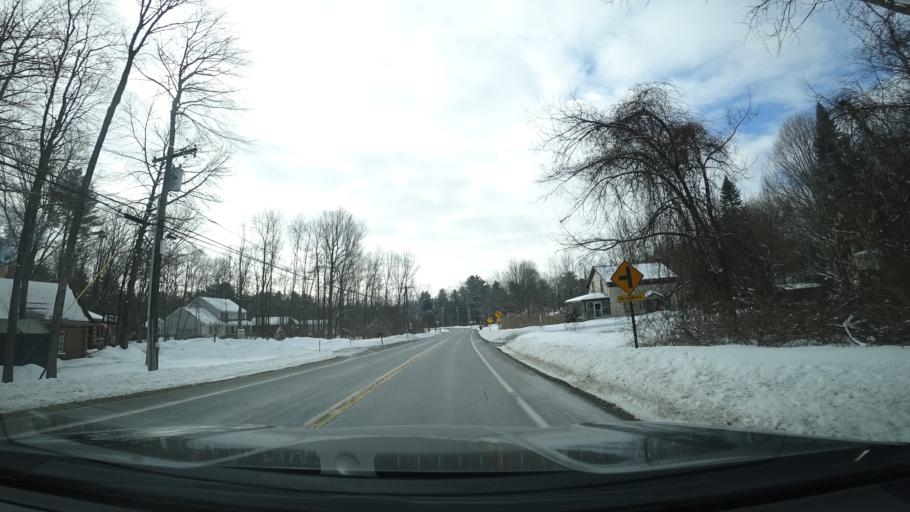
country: US
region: New York
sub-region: Saratoga County
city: South Glens Falls
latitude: 43.2820
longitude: -73.6184
